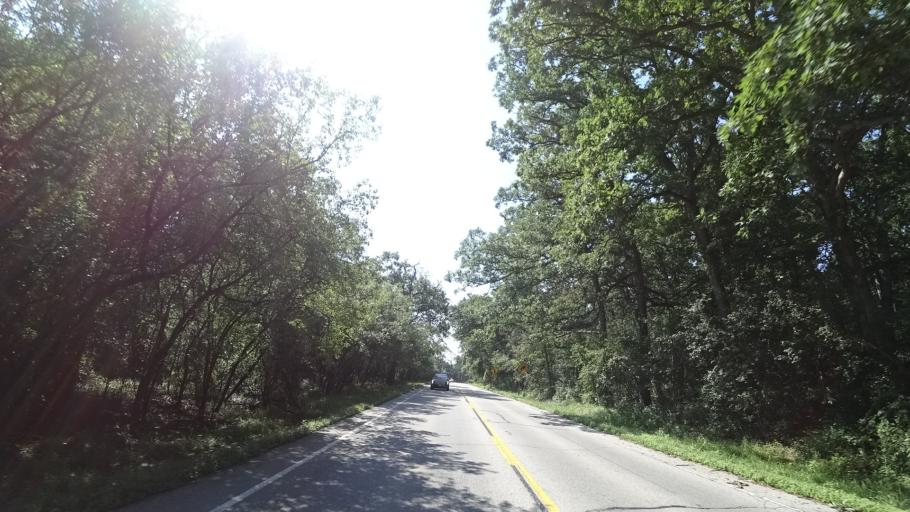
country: US
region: Illinois
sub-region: Cook County
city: Oak Forest
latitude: 41.5822
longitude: -87.7553
